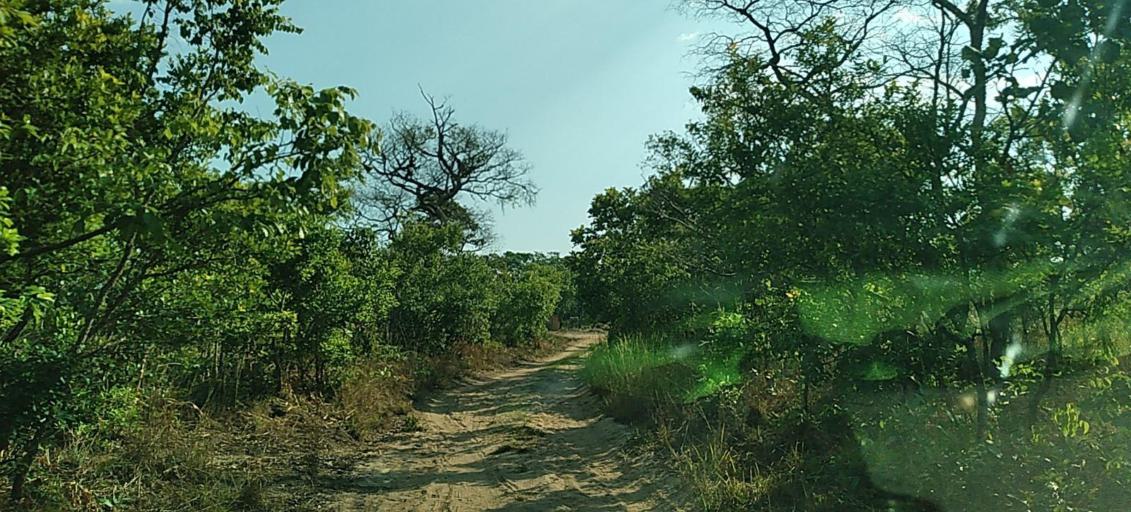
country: ZM
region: North-Western
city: Mwinilunga
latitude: -11.3285
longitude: 24.7373
